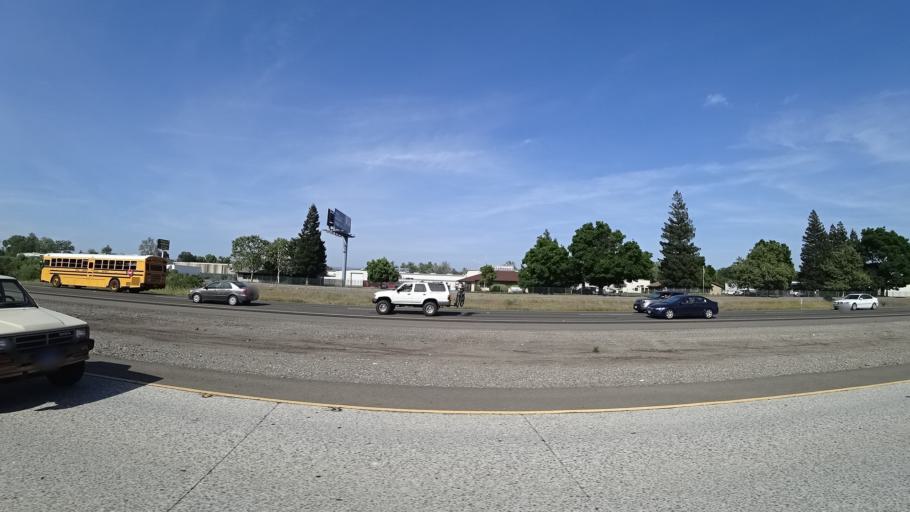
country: US
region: California
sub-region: Butte County
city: Durham
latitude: 39.6972
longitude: -121.7816
